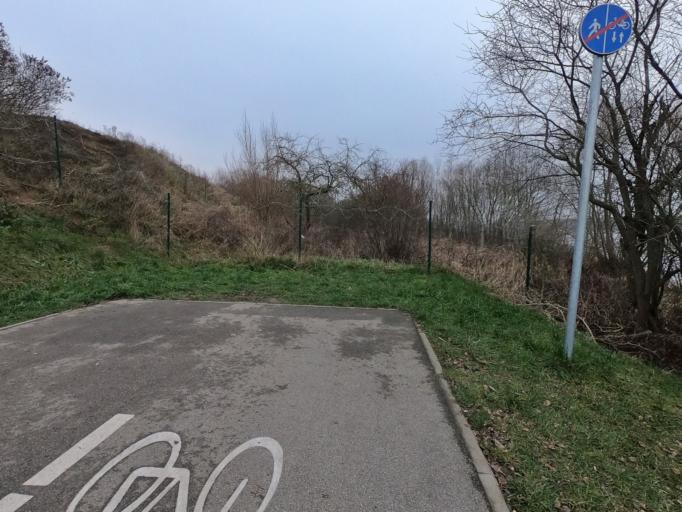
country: LV
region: Kekava
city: Kekava
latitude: 56.8794
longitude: 24.2207
